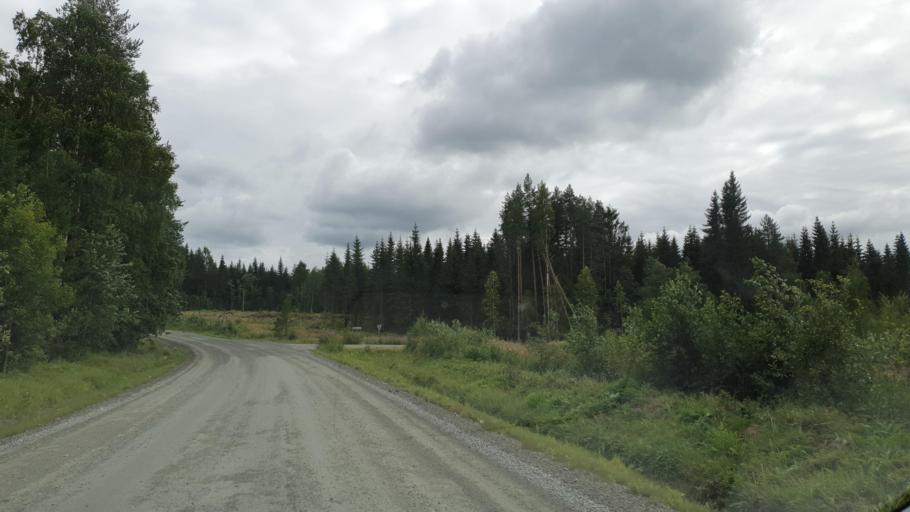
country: FI
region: Northern Savo
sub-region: Ylae-Savo
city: Iisalmi
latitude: 63.5274
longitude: 27.0889
